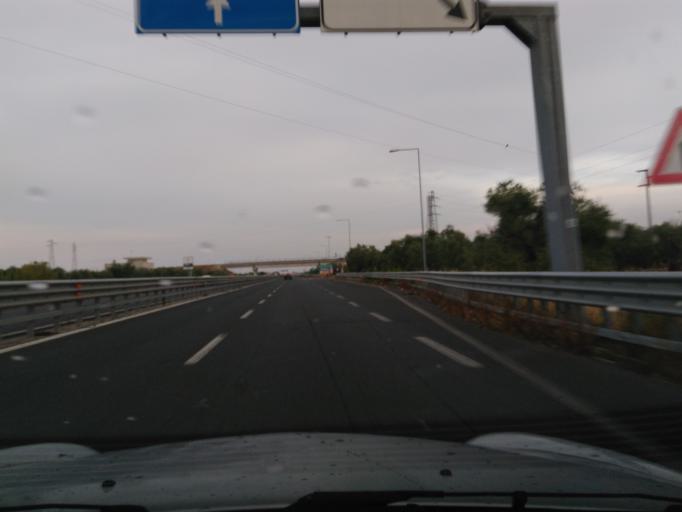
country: IT
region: Apulia
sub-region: Provincia di Bari
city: Giovinazzo
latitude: 41.1740
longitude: 16.6700
